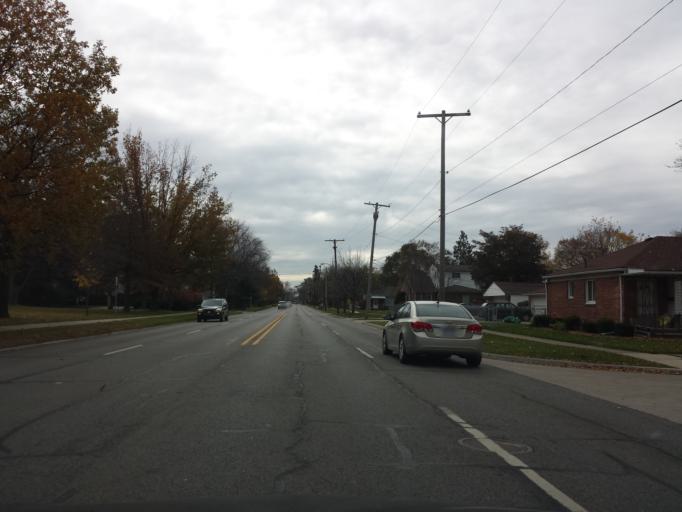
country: US
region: Michigan
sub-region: Oakland County
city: Clawson
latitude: 42.5256
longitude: -83.1459
